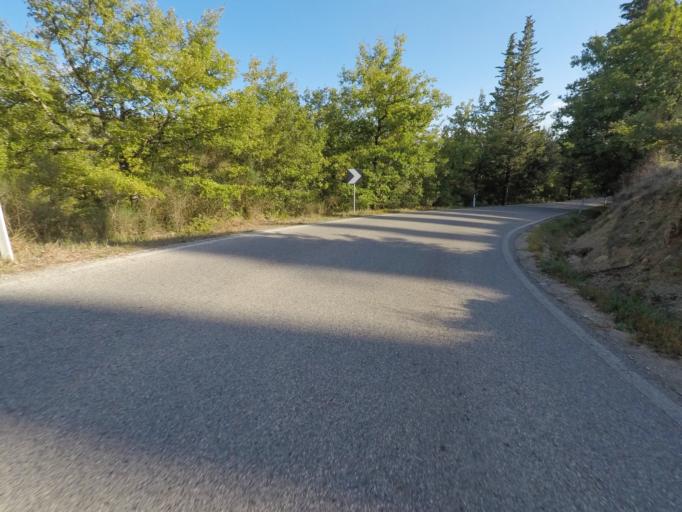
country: IT
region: Tuscany
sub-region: Provincia di Siena
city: Radda in Chianti
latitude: 43.4765
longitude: 11.3737
